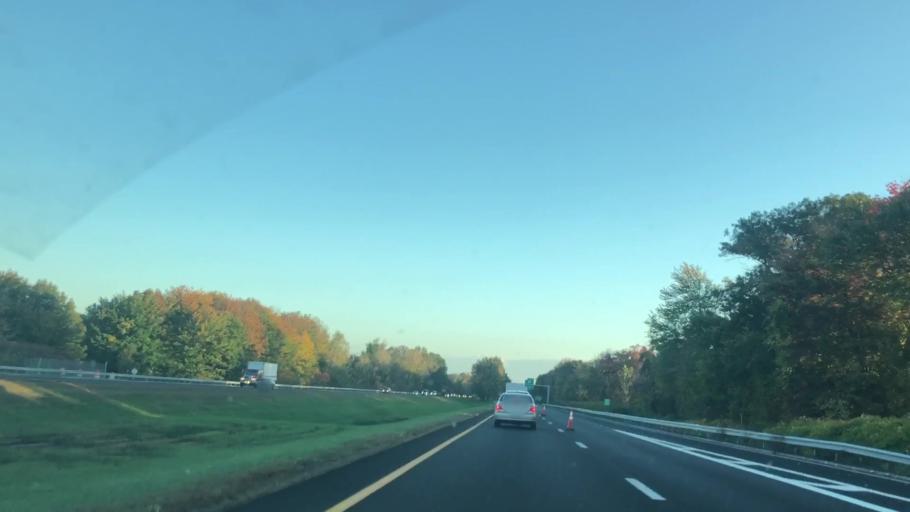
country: US
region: Massachusetts
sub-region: Franklin County
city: South Deerfield
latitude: 42.5037
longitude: -72.6200
